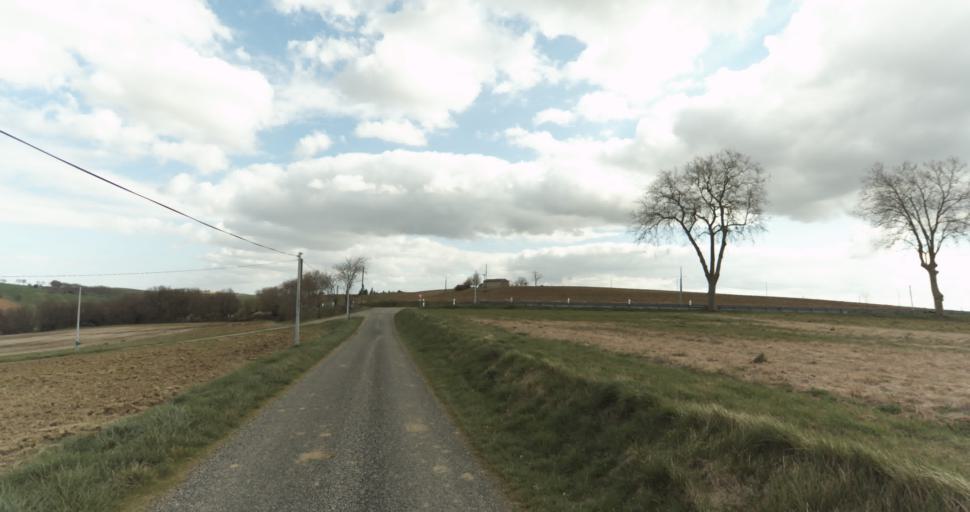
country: FR
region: Midi-Pyrenees
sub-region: Departement de la Haute-Garonne
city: Auterive
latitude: 43.3602
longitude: 1.4973
